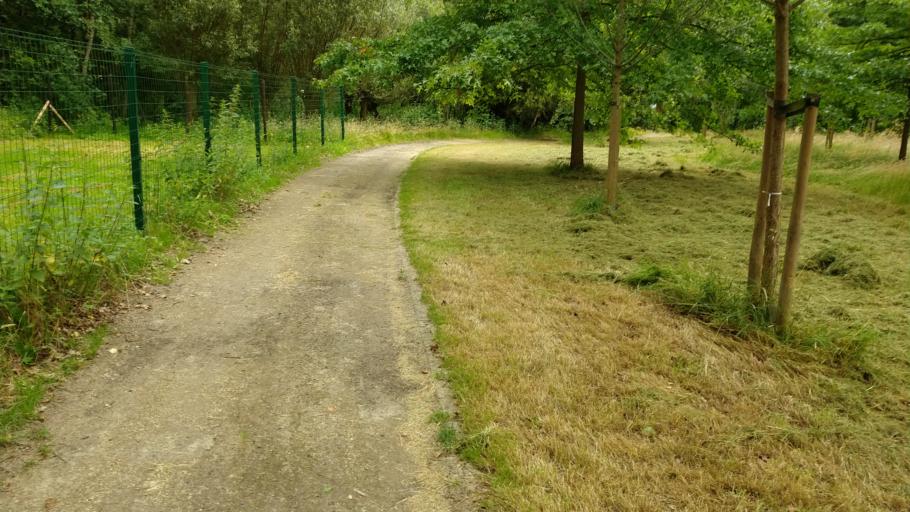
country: BE
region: Flanders
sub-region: Provincie Vlaams-Brabant
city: Diest
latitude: 50.9829
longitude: 5.0669
